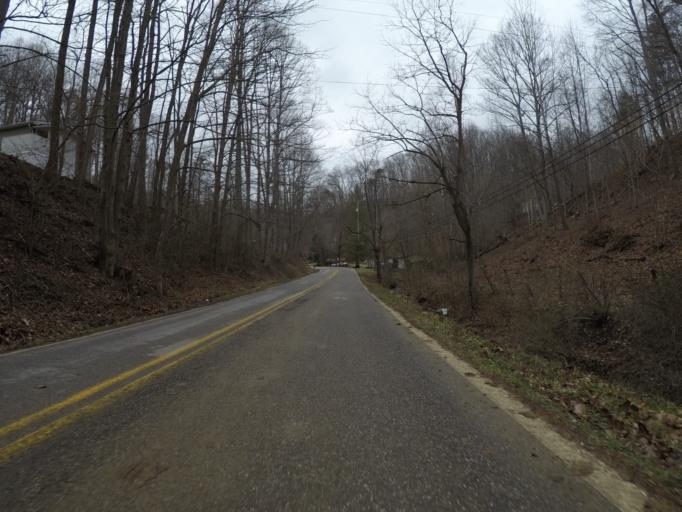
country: US
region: West Virginia
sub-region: Cabell County
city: Lesage
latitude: 38.4599
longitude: -82.2706
